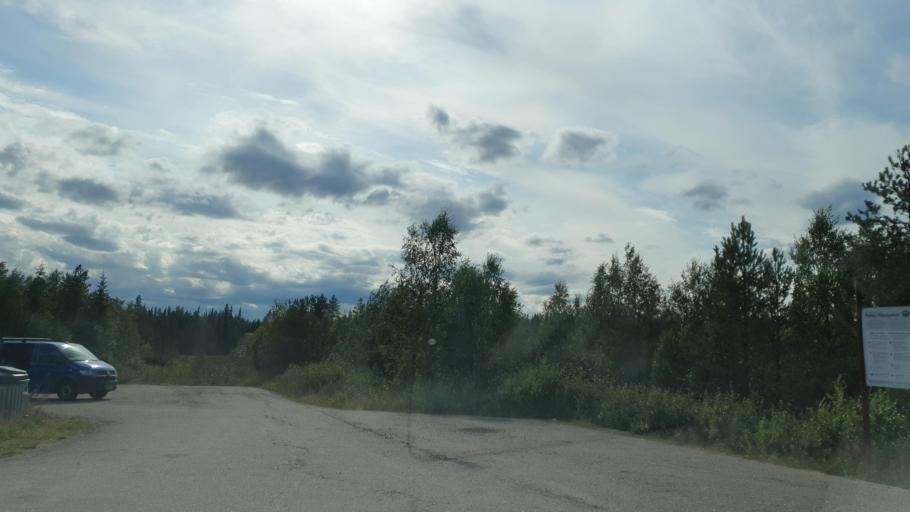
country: FI
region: Lapland
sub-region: Tunturi-Lappi
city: Muonio
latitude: 67.7068
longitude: 24.1262
